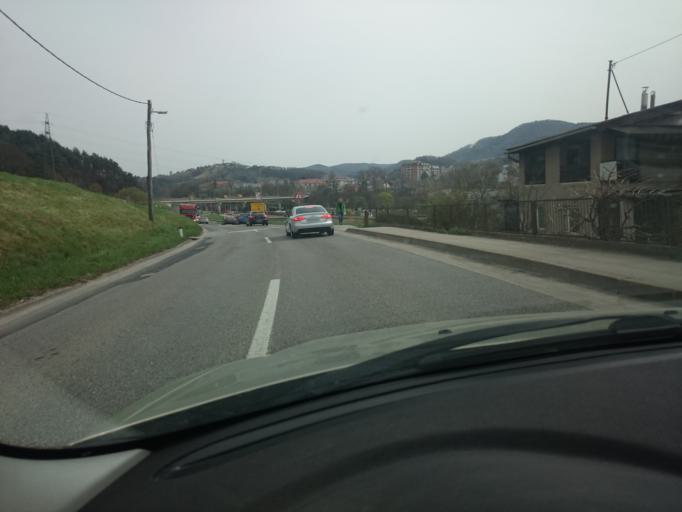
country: SI
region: Store
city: Store
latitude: 46.2264
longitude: 15.3061
